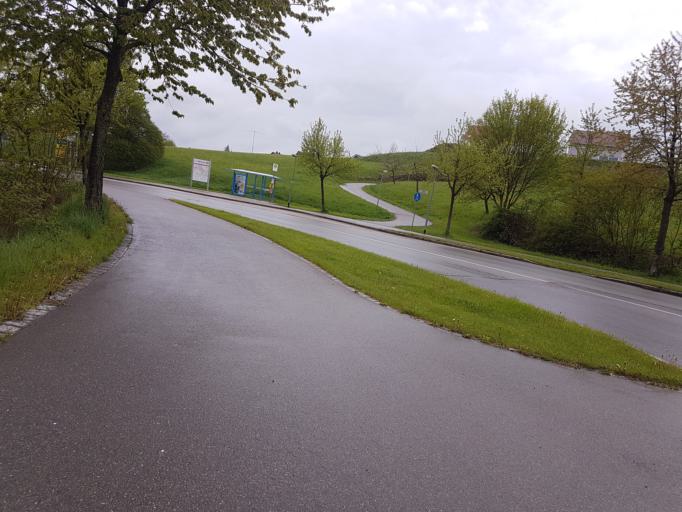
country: DE
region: Baden-Wuerttemberg
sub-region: Freiburg Region
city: Rottweil
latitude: 48.1741
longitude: 8.6119
